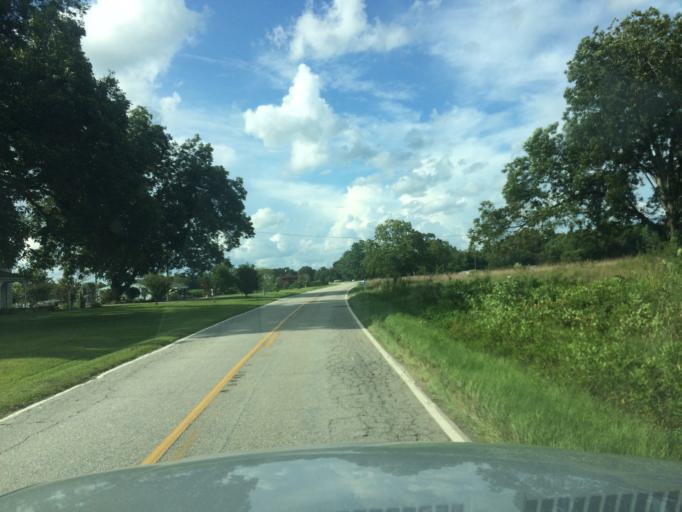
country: US
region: South Carolina
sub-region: Spartanburg County
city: Woodruff
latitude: 34.7719
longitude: -82.1116
